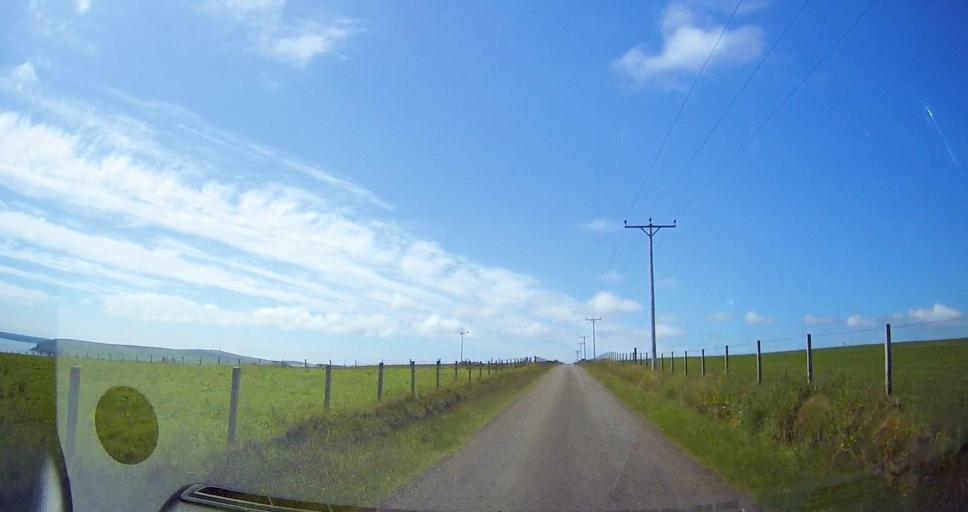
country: GB
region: Scotland
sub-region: Orkney Islands
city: Kirkwall
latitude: 58.8153
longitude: -2.9171
